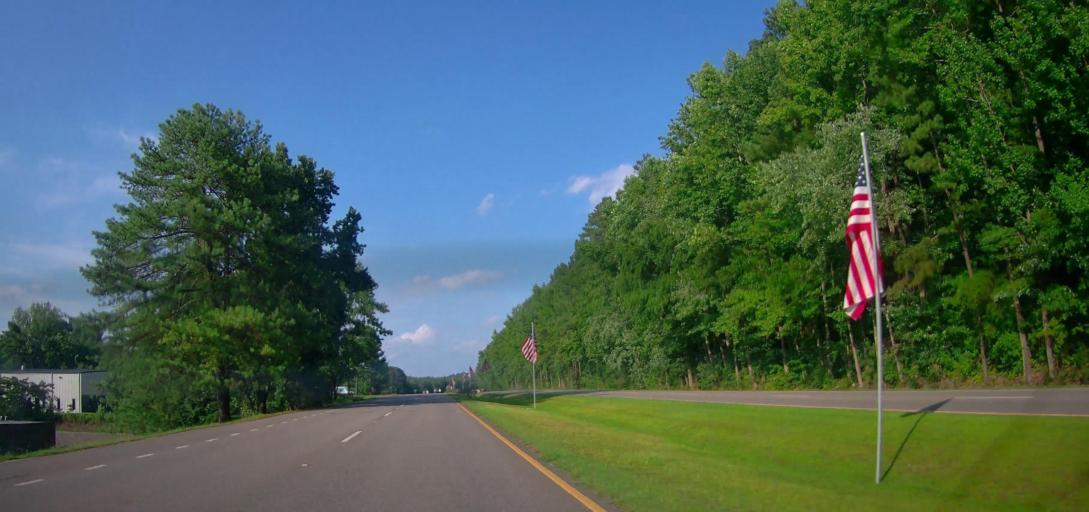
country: US
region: Alabama
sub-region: Jefferson County
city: Irondale
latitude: 33.5422
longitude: -86.6886
